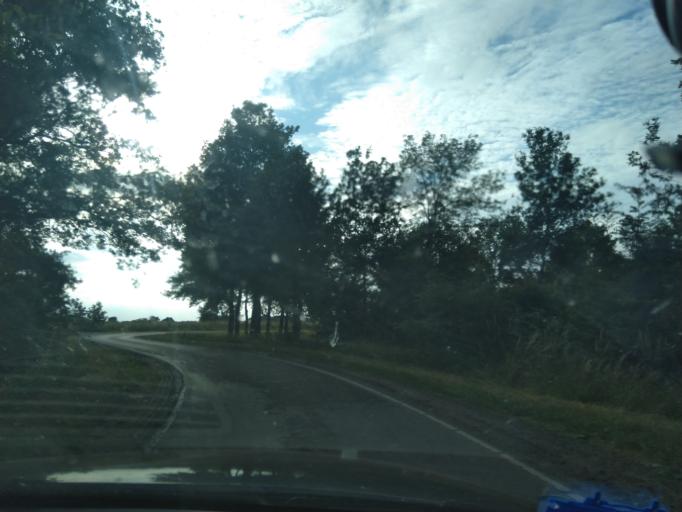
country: NL
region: Groningen
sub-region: Gemeente Vlagtwedde
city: Vlagtwedde
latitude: 53.0895
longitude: 7.1007
